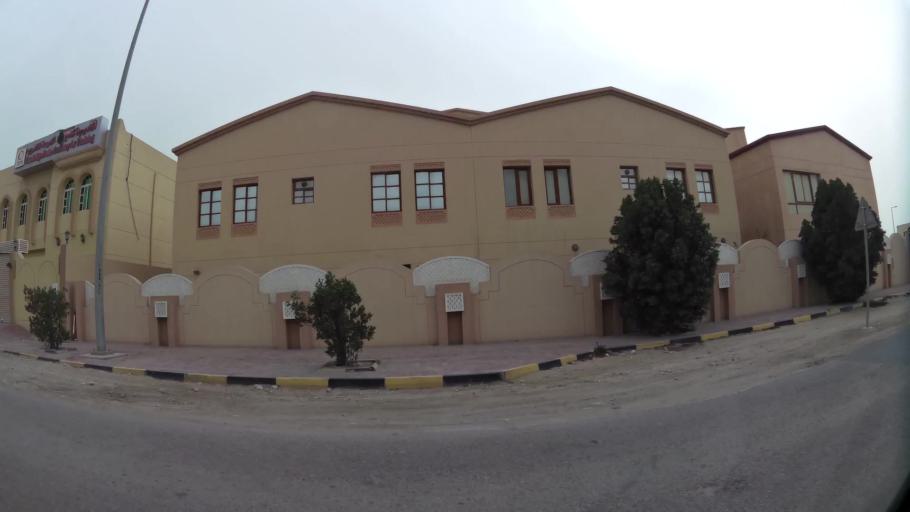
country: QA
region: Baladiyat ad Dawhah
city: Doha
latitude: 25.2441
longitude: 51.5087
